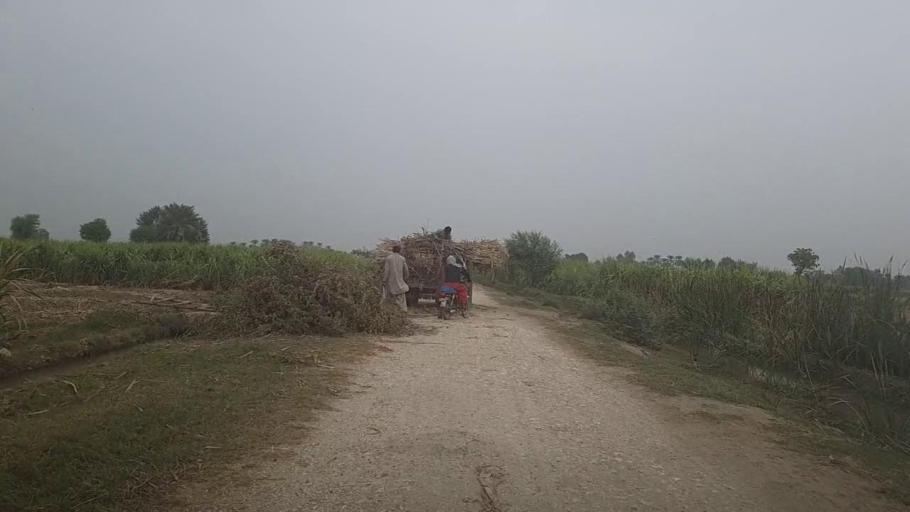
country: PK
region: Sindh
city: Gambat
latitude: 27.3089
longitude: 68.6068
